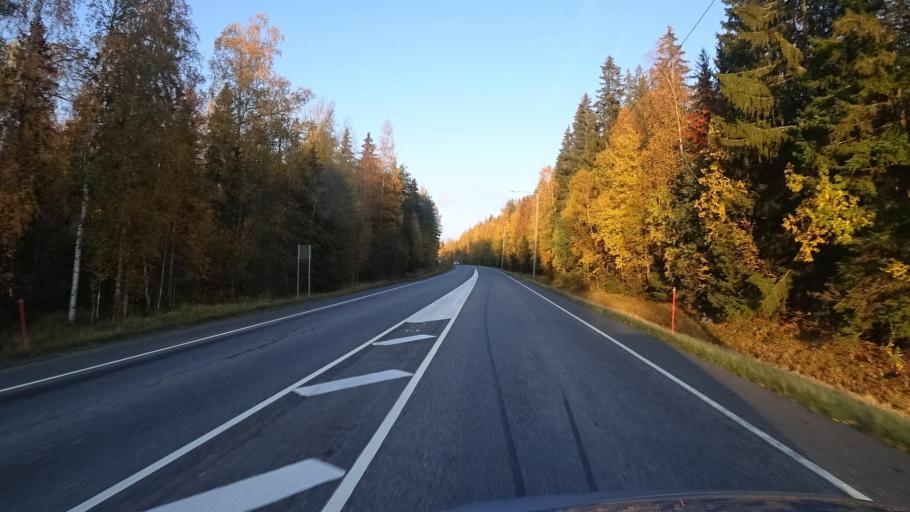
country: FI
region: Haeme
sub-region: Forssa
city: Jokioinen
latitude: 60.7898
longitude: 23.4940
